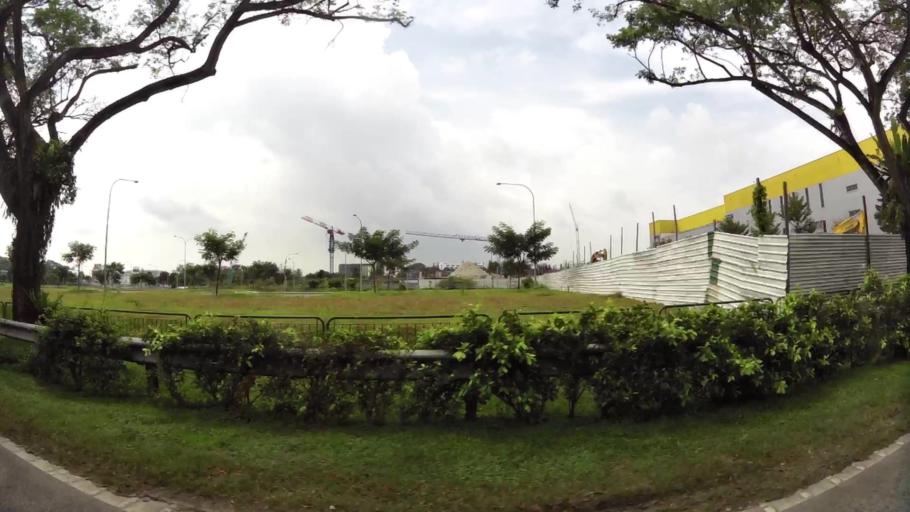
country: MY
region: Johor
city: Kampung Pasir Gudang Baru
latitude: 1.3741
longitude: 103.9349
